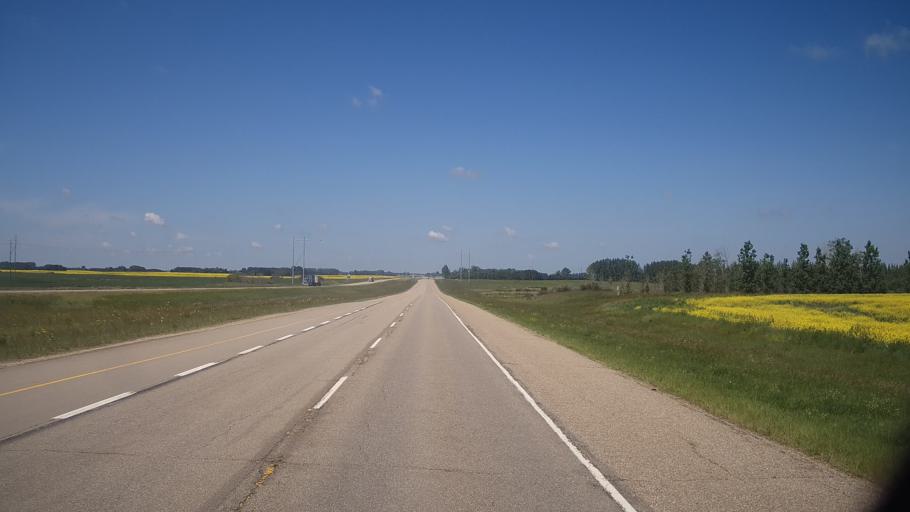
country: CA
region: Saskatchewan
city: Saskatoon
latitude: 51.9981
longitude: -106.3003
